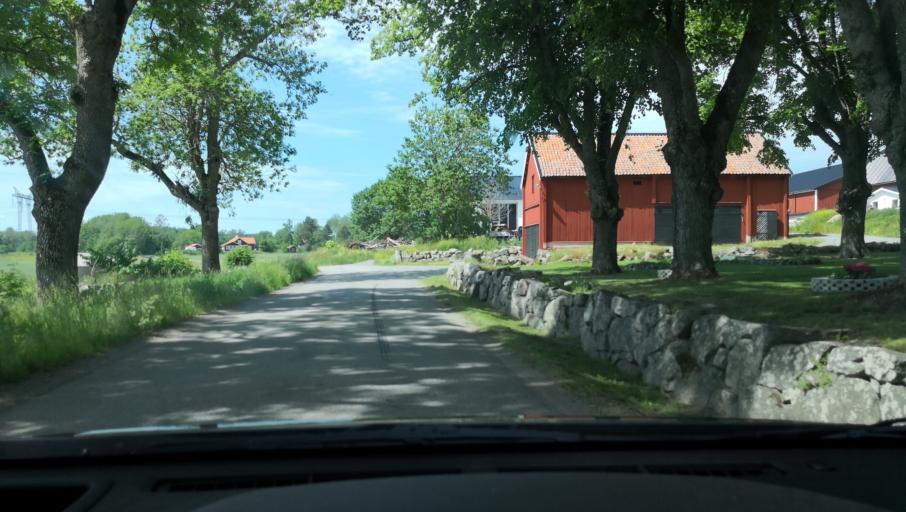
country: SE
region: Stockholm
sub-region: Sigtuna Kommun
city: Sigtuna
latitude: 59.6795
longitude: 17.6925
